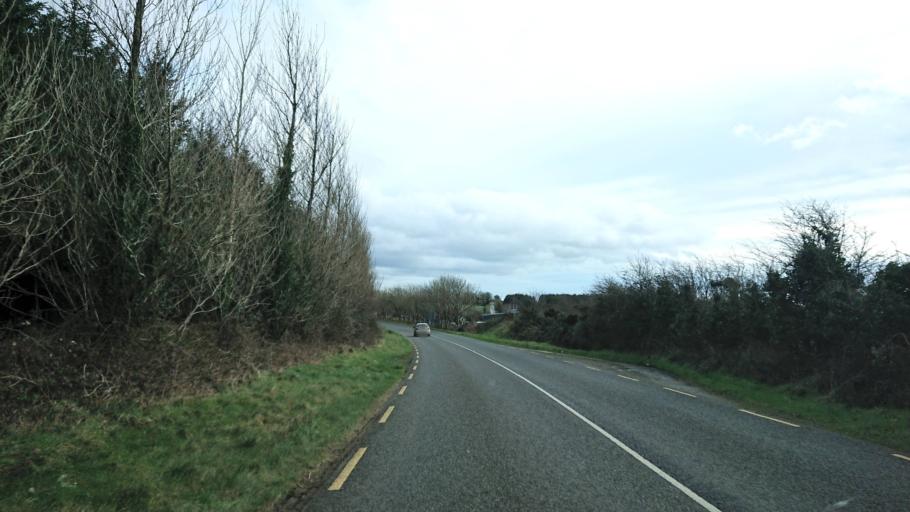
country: IE
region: Munster
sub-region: Waterford
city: Dunmore East
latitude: 52.2415
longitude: -6.8910
